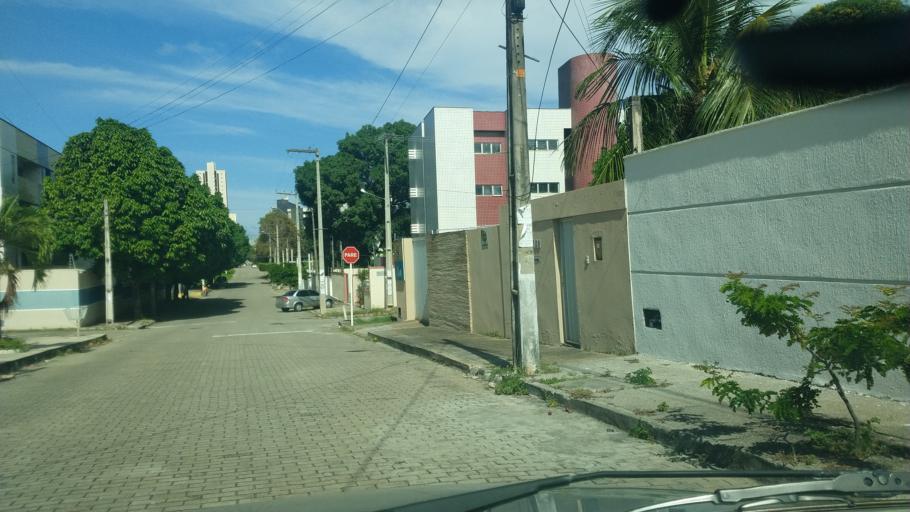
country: BR
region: Rio Grande do Norte
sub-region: Natal
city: Natal
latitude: -5.8599
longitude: -35.2000
